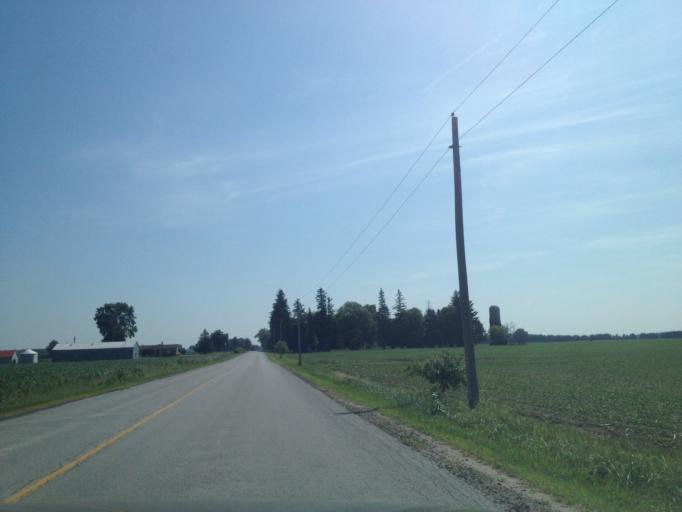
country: CA
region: Ontario
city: London
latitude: 43.1220
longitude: -81.2348
